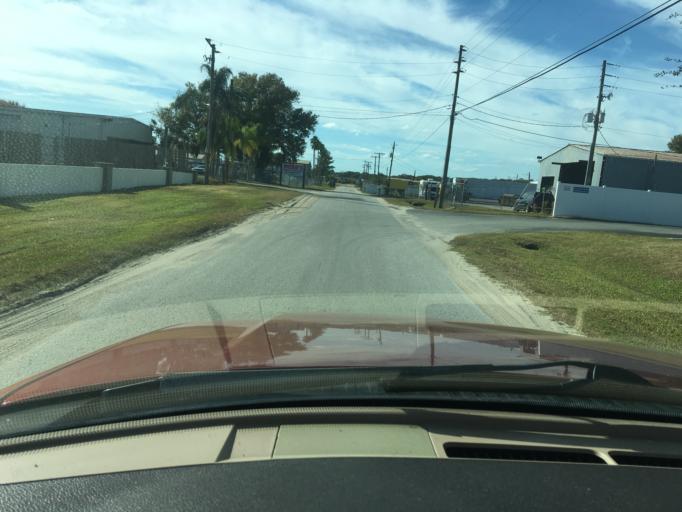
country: US
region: Florida
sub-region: Polk County
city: Mulberry
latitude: 27.9113
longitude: -81.9794
